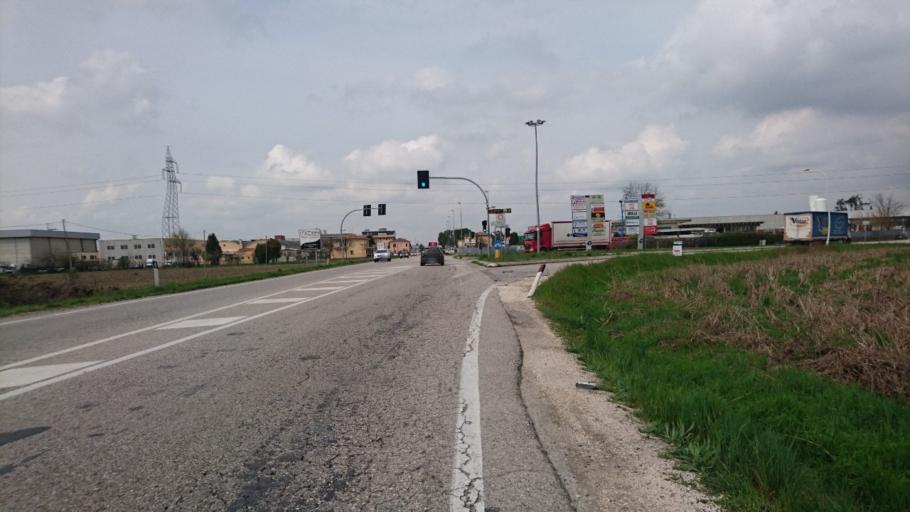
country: IT
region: Veneto
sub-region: Provincia di Padova
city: Limena
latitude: 45.4554
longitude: 11.8570
